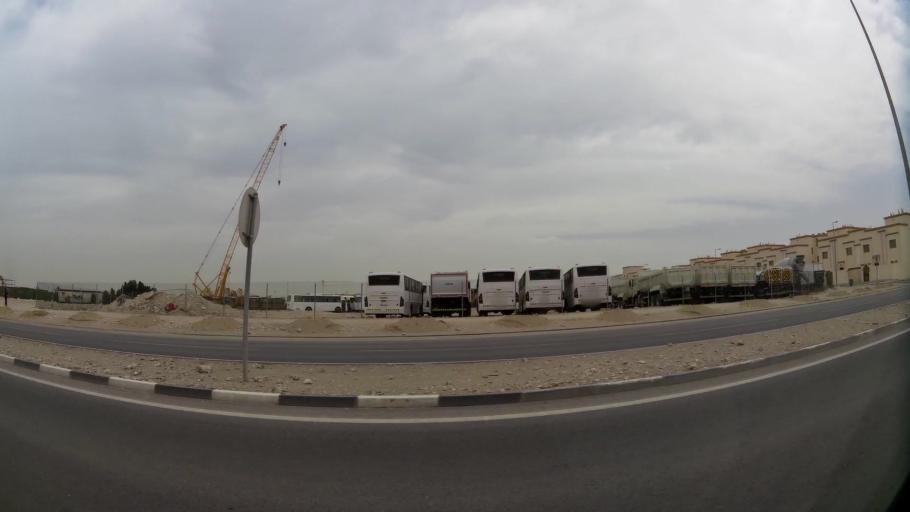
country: QA
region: Baladiyat ad Dawhah
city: Doha
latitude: 25.2291
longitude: 51.4703
